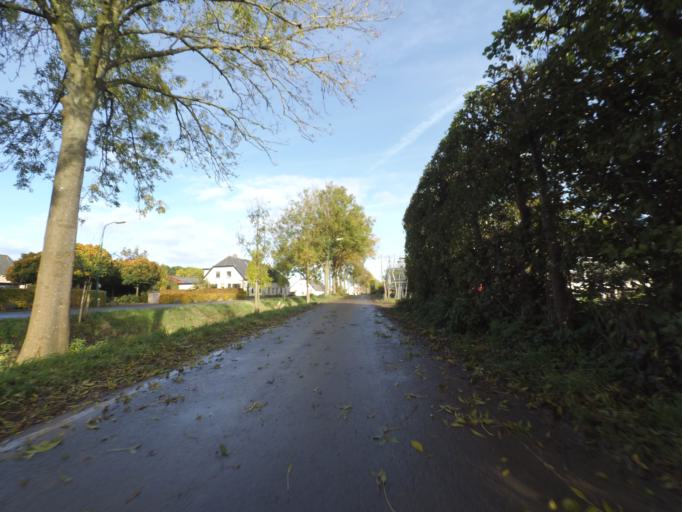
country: NL
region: Utrecht
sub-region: Gemeente Wijk bij Duurstede
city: Wijk bij Duurstede
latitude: 51.9882
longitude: 5.2819
